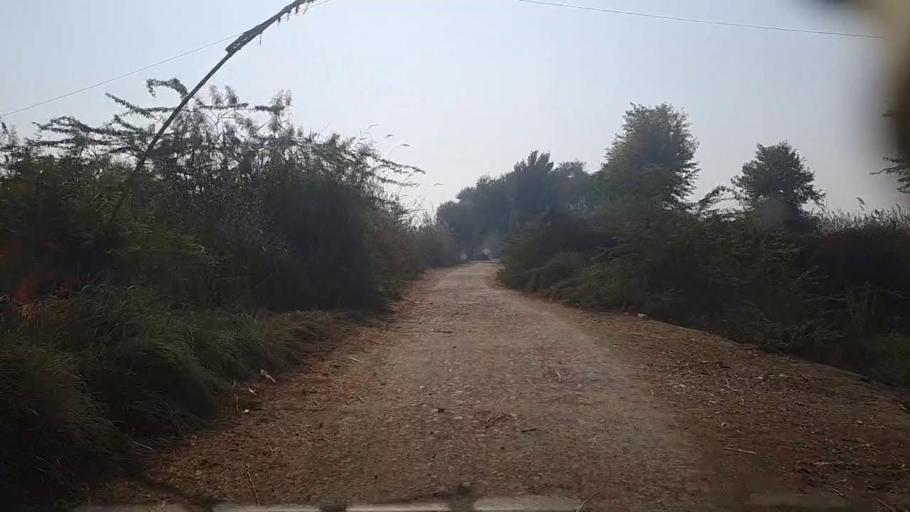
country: PK
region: Sindh
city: Kandiari
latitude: 26.9783
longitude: 68.4694
